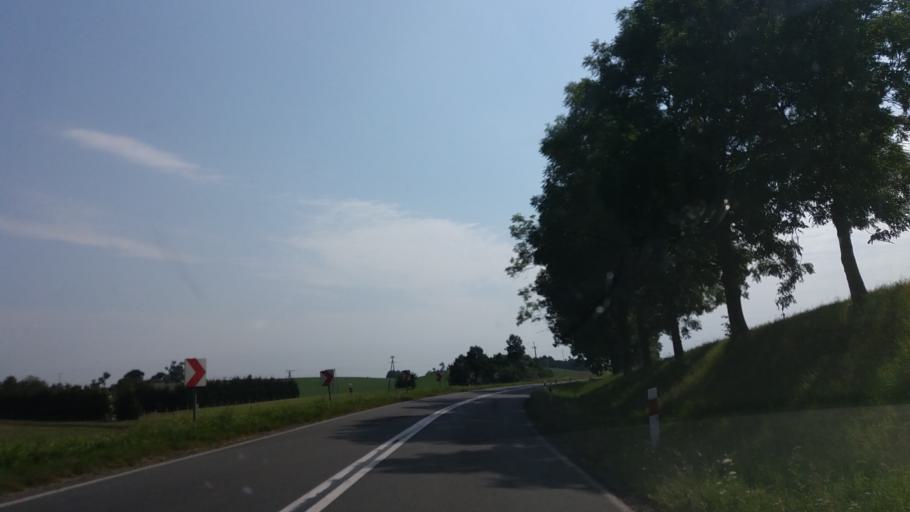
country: PL
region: Lubusz
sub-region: Powiat strzelecko-drezdenecki
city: Strzelce Krajenskie
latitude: 52.8606
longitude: 15.5404
